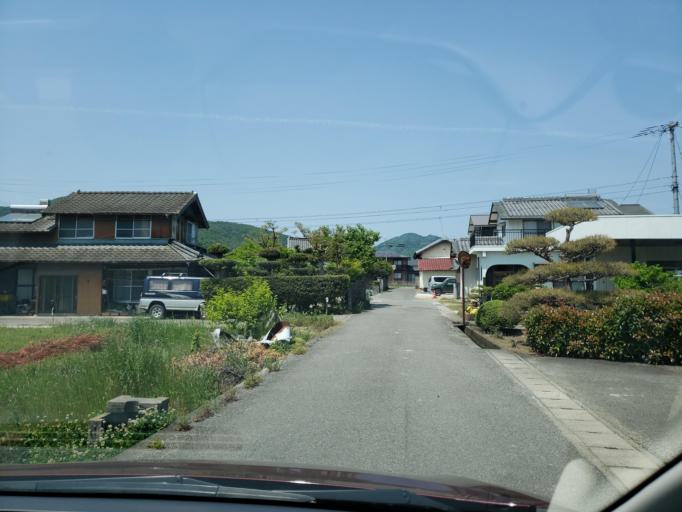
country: JP
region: Tokushima
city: Kamojimacho-jogejima
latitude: 34.0950
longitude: 134.2682
